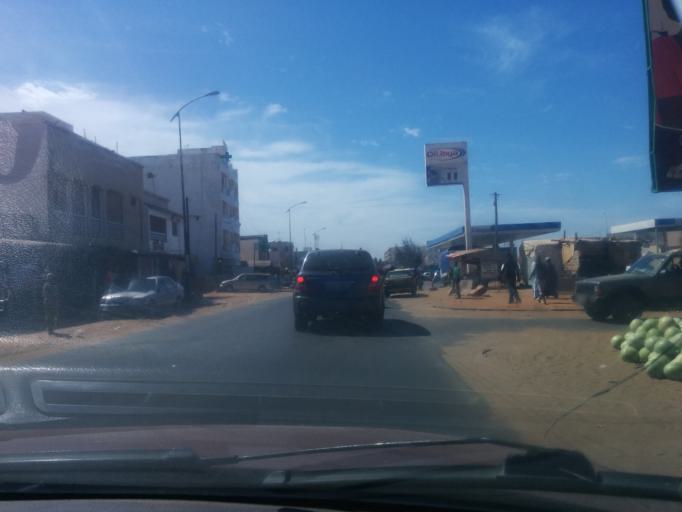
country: SN
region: Dakar
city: Pikine
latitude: 14.7700
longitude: -17.4095
